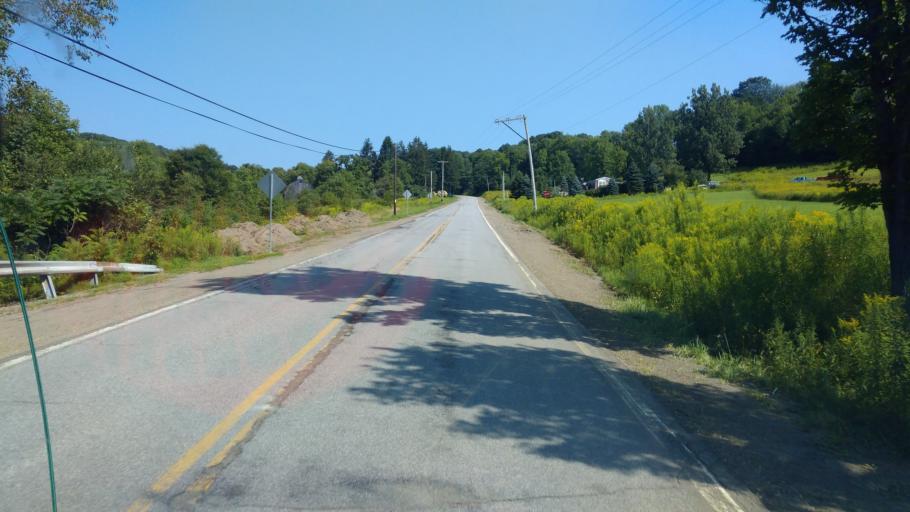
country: US
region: New York
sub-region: Allegany County
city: Bolivar
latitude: 42.1023
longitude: -78.1756
